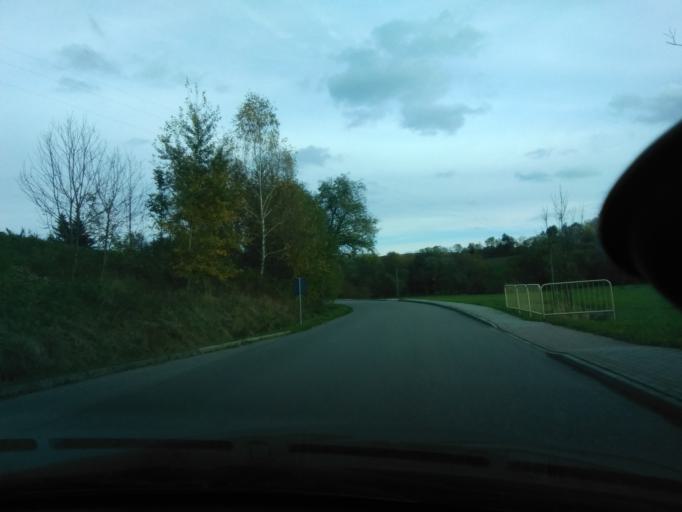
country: PL
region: Subcarpathian Voivodeship
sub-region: Powiat ropczycko-sedziszowski
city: Wielopole Skrzynskie
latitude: 49.9312
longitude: 21.5542
